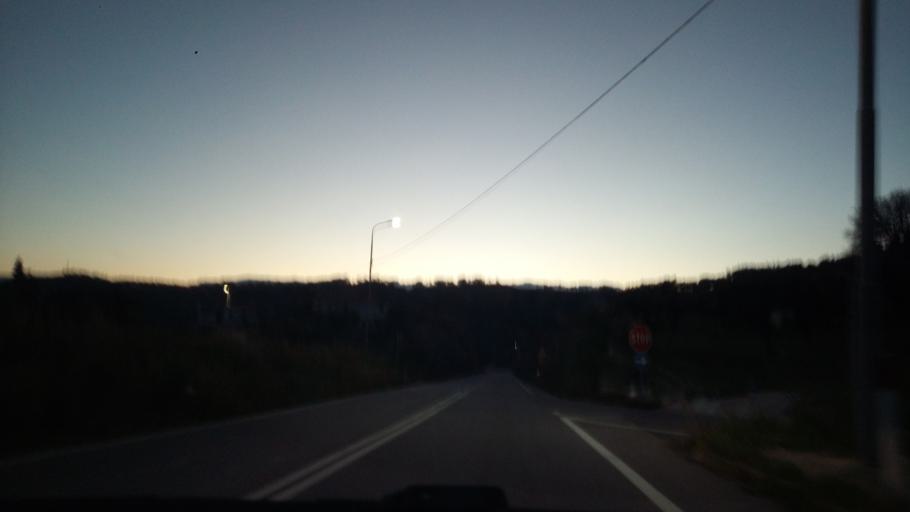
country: IT
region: Calabria
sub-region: Provincia di Catanzaro
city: Cava-Cuculera Nobile
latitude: 38.8977
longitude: 16.6211
